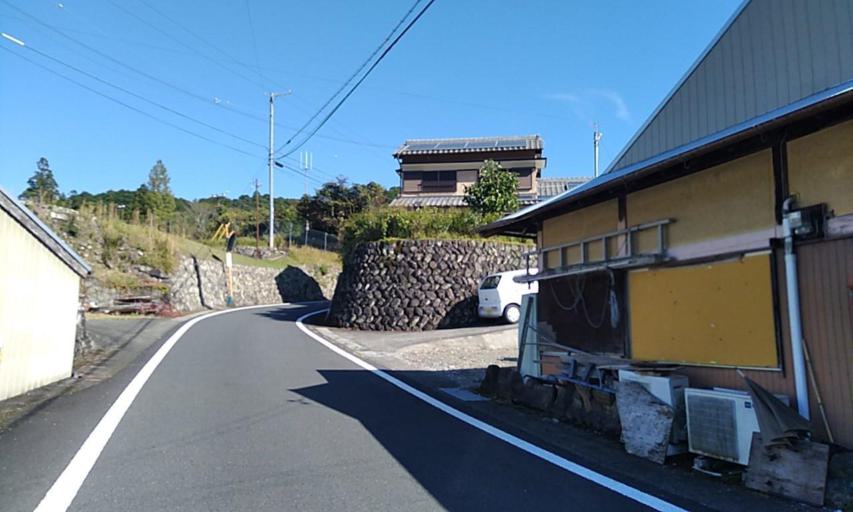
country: JP
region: Wakayama
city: Shingu
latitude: 33.9233
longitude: 135.9832
